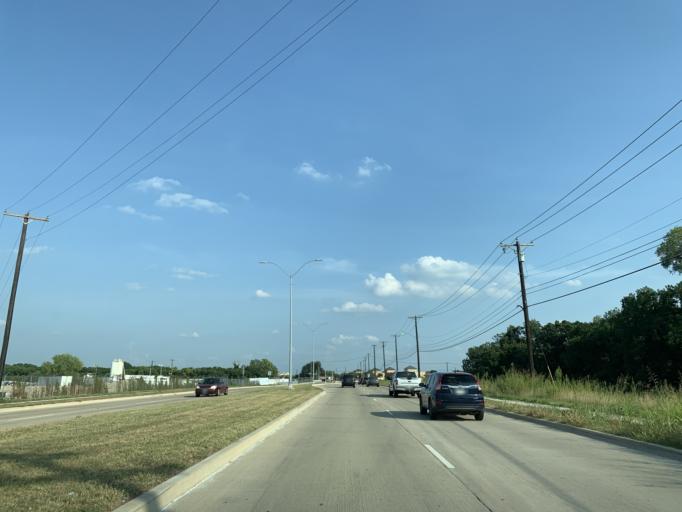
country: US
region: Texas
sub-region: Tarrant County
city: Hurst
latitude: 32.8053
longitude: -97.1862
